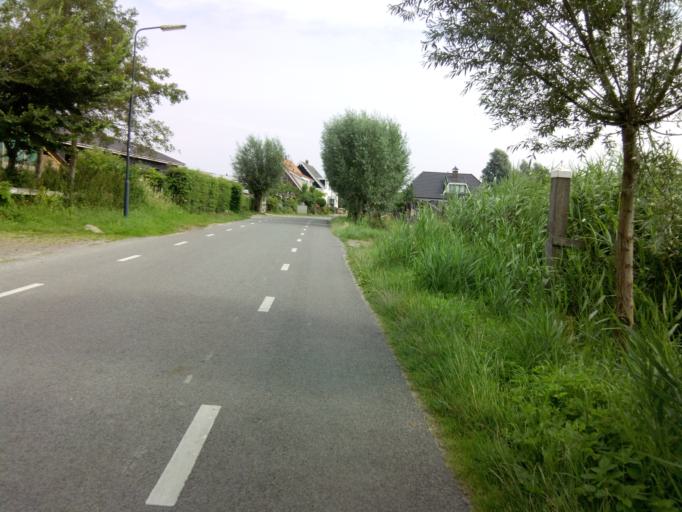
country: NL
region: Utrecht
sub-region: Gemeente Bunschoten
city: Spakenburg
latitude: 52.2608
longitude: 5.3353
